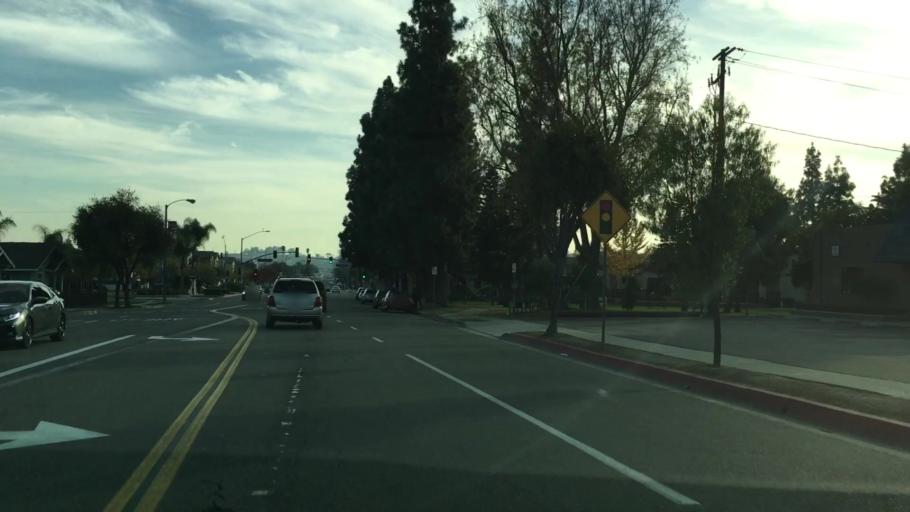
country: US
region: California
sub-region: Orange County
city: La Habra
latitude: 33.9307
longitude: -117.9462
